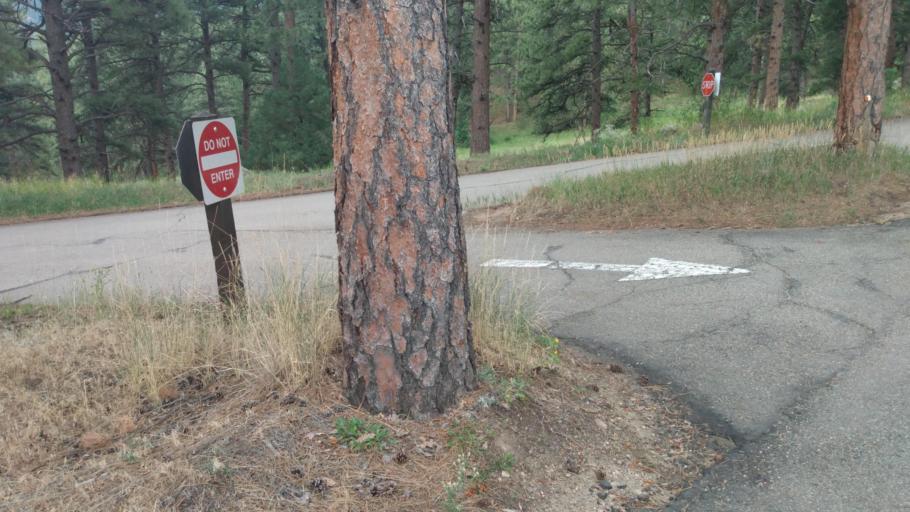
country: US
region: Colorado
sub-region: Boulder County
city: Boulder
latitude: 40.0039
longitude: -105.3040
